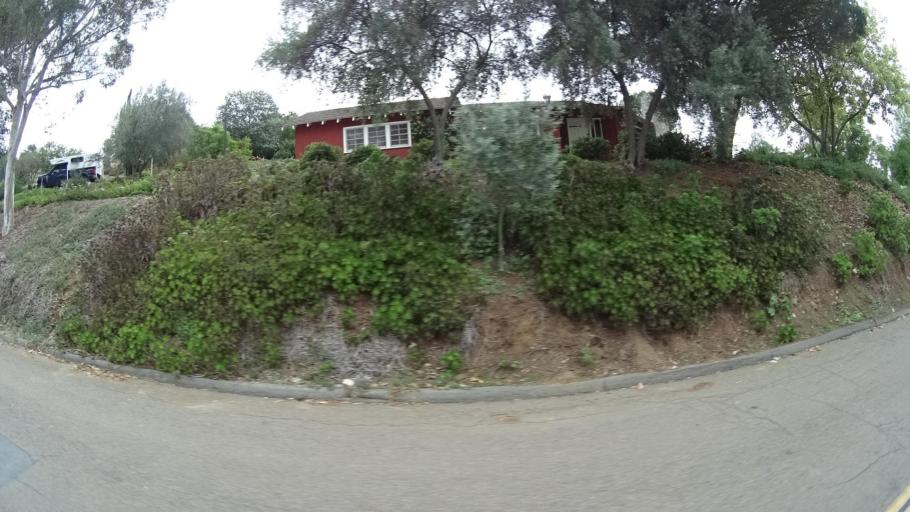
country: US
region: California
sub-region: San Diego County
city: Spring Valley
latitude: 32.7475
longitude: -117.0097
